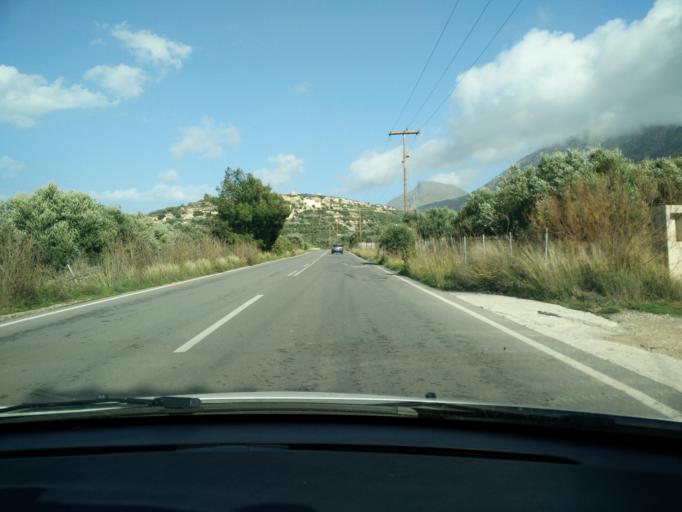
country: GR
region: Crete
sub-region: Nomos Lasithiou
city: Kato Chorio
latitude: 35.0573
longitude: 25.7968
